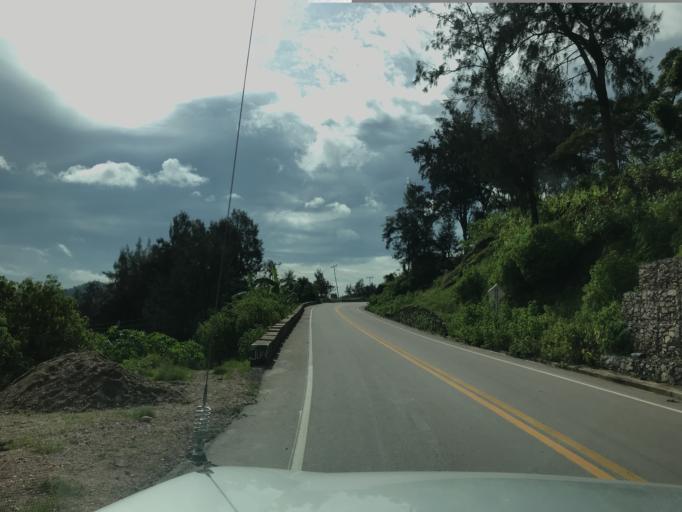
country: TL
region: Aileu
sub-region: Aileu Villa
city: Aileu
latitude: -8.8108
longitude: 125.5963
